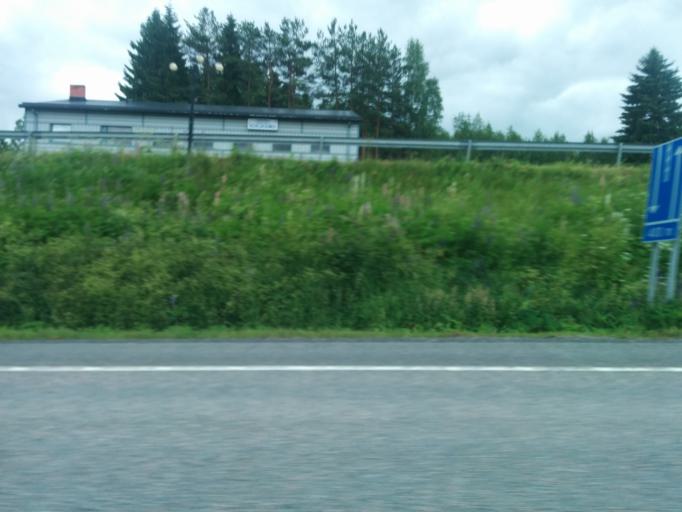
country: FI
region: Pirkanmaa
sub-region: Tampere
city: Orivesi
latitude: 61.7016
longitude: 24.4359
